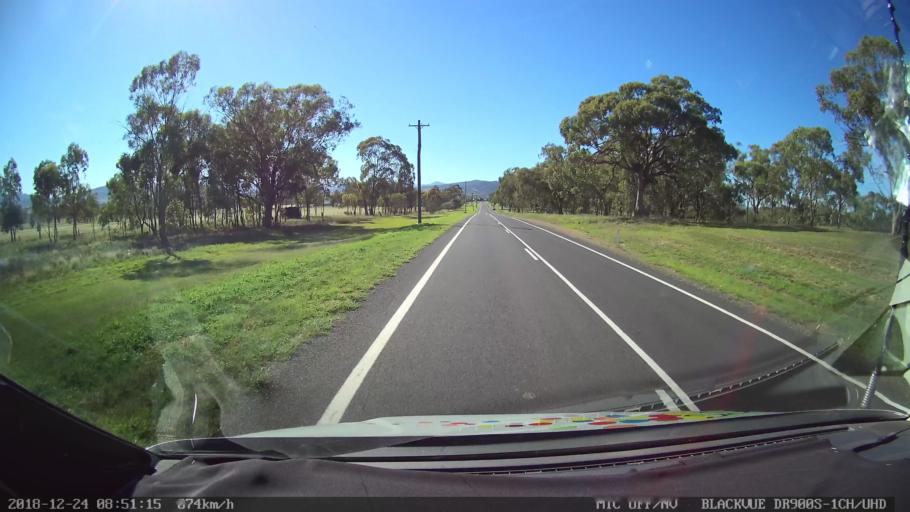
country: AU
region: New South Wales
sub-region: Liverpool Plains
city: Quirindi
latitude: -31.4828
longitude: 150.6726
